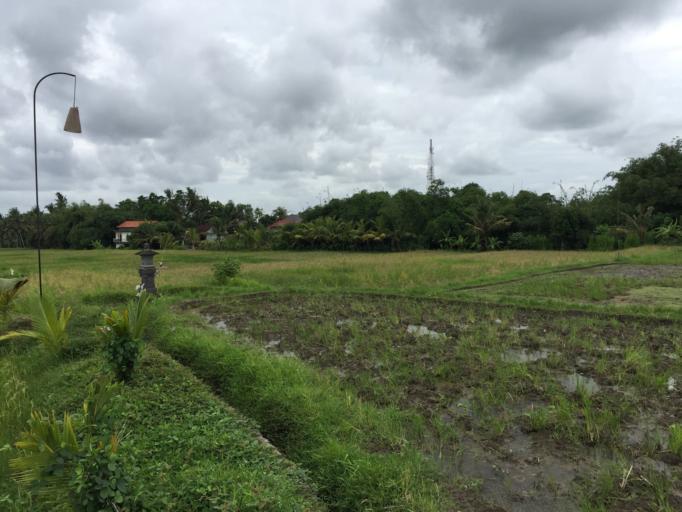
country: ID
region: Bali
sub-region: Kabupaten Gianyar
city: Ubud
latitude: -8.5250
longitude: 115.2757
